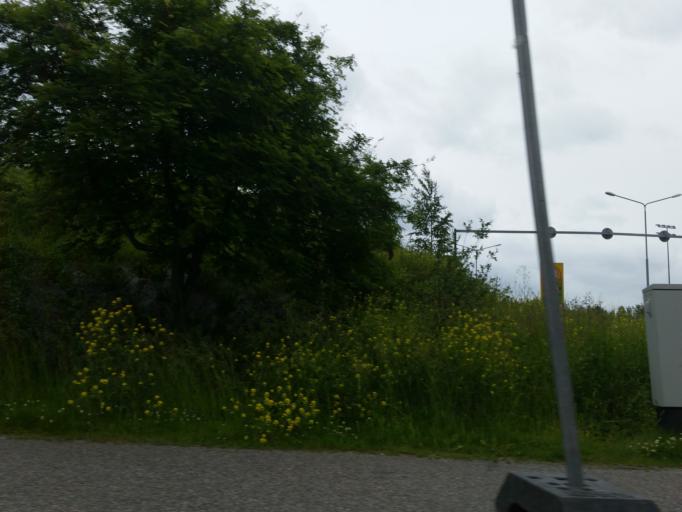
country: FI
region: Northern Savo
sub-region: Kuopio
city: Kuopio
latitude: 62.8872
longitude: 27.6298
